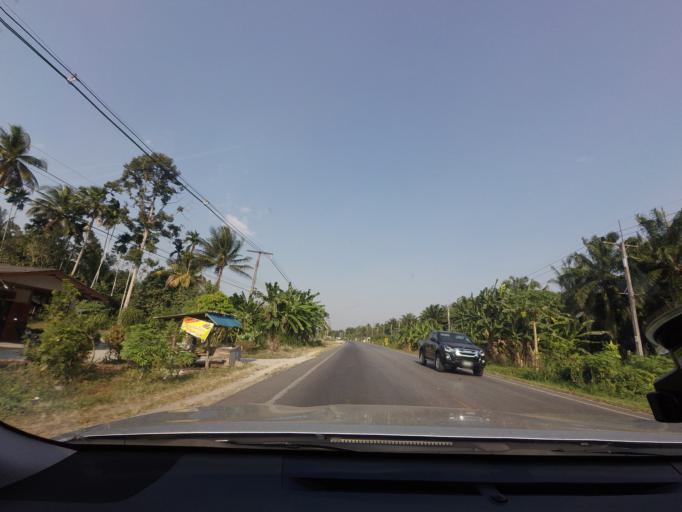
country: TH
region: Surat Thani
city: Phrasaeng
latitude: 8.5666
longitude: 99.1883
